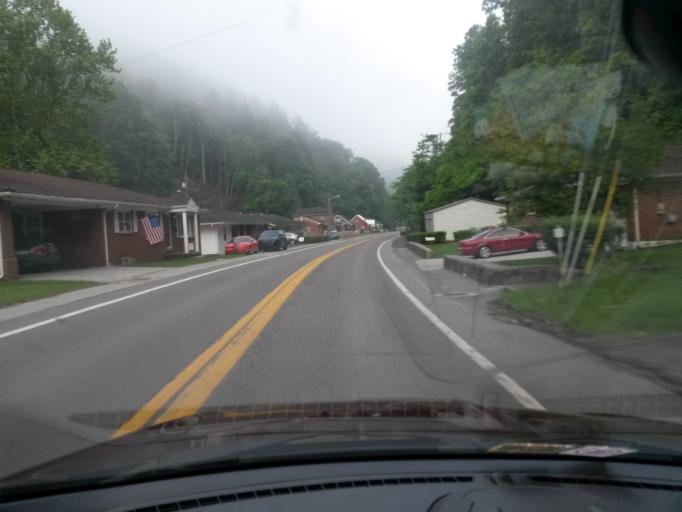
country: US
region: West Virginia
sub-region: McDowell County
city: Welch
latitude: 37.4445
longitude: -81.5670
